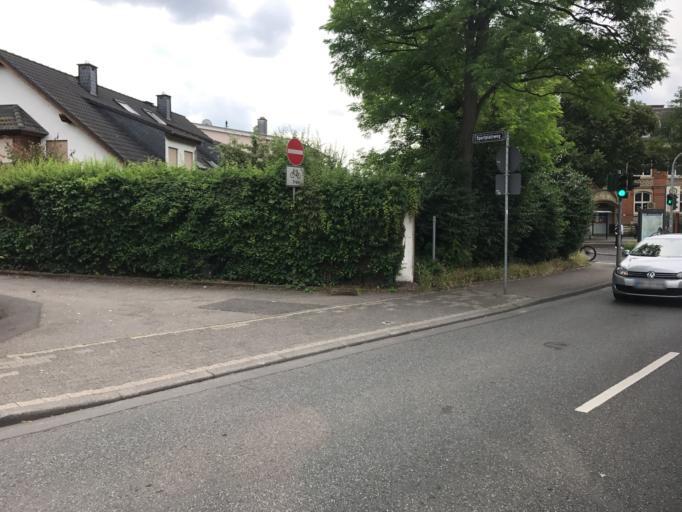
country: DE
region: Rheinland-Pfalz
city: Budenheim
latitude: 50.0465
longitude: 8.2009
